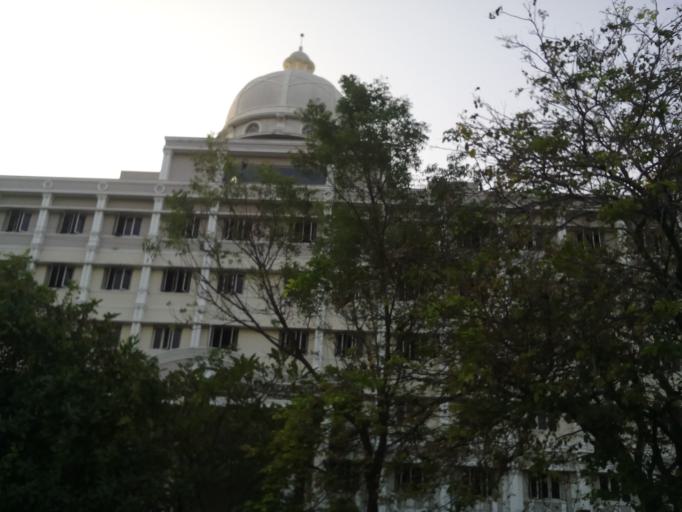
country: IN
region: Tamil Nadu
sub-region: Thanjavur
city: Kumbakonam
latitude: 10.9636
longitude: 79.3864
